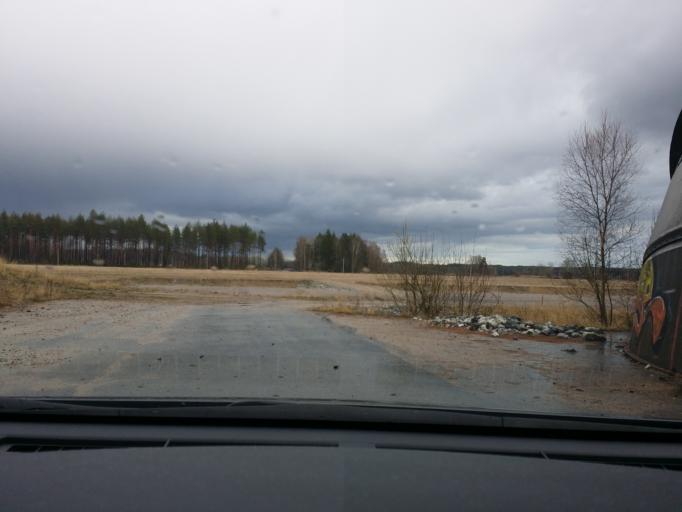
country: SE
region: Soedermanland
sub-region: Eskilstuna Kommun
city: Arla
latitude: 59.3442
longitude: 16.6924
